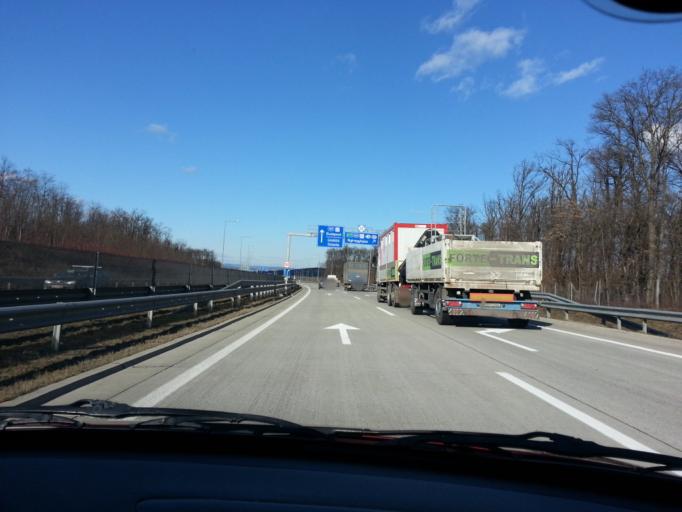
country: HU
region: Pest
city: Szada
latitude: 47.6042
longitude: 19.3208
